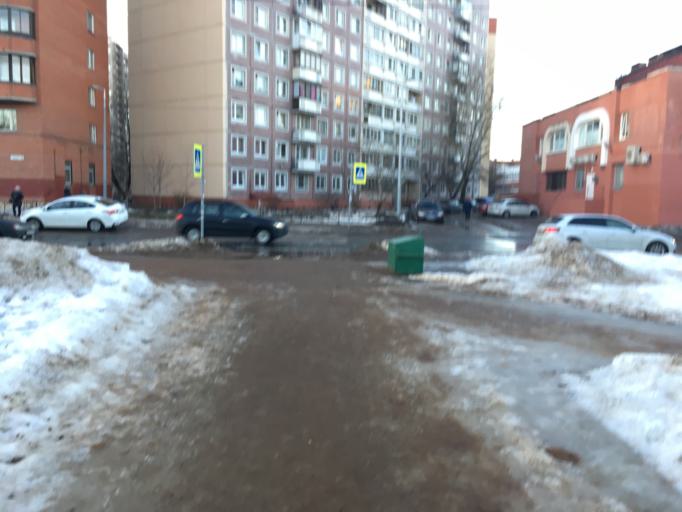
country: RU
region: St.-Petersburg
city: Komendantsky aerodrom
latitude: 60.0182
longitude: 30.2507
